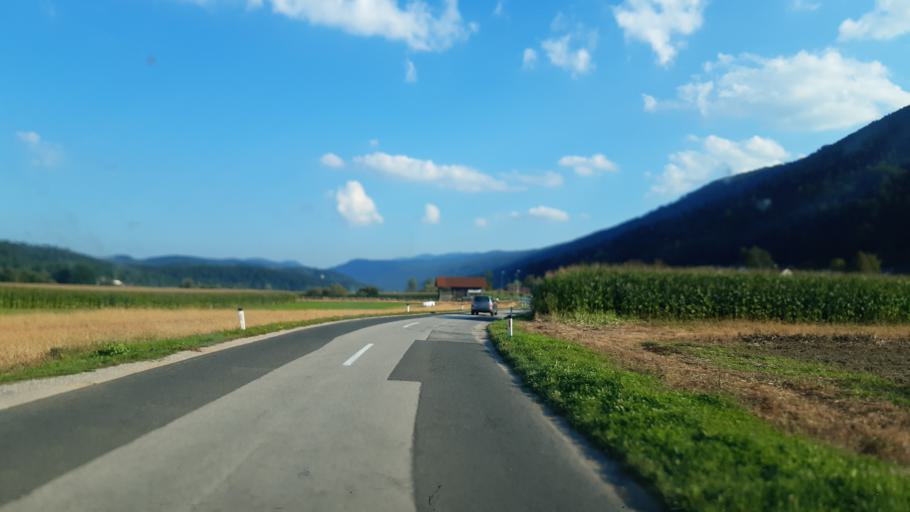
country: SI
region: Dolenjske Toplice
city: Dolenjske Toplice
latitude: 45.7538
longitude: 15.0343
